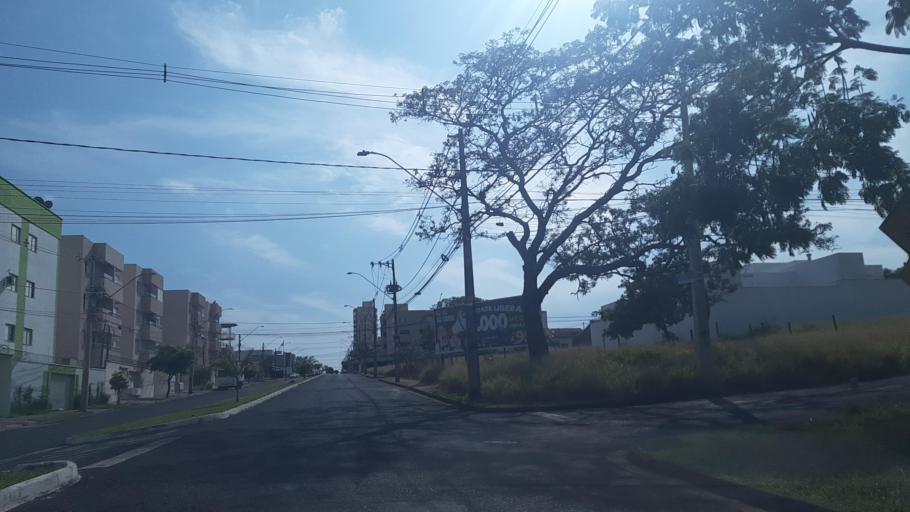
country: BR
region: Minas Gerais
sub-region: Uberlandia
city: Uberlandia
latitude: -18.8766
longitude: -48.2358
